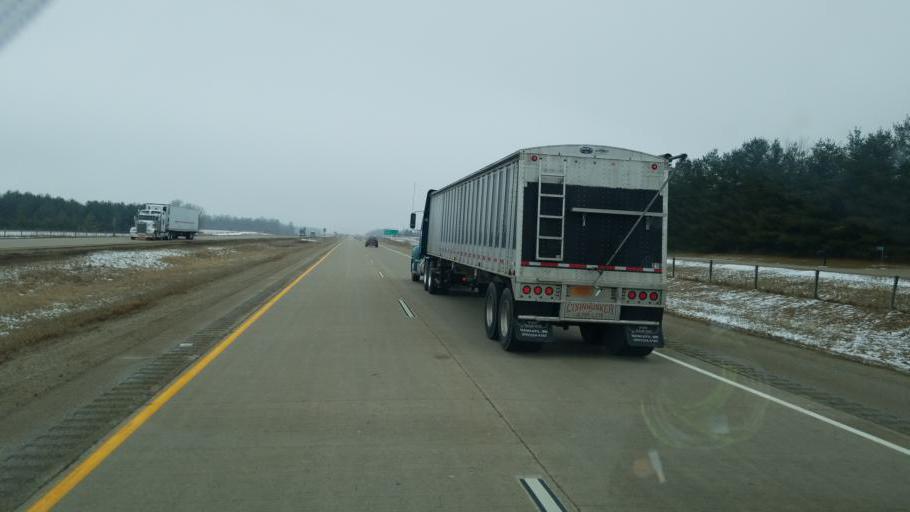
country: US
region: Wisconsin
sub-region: Winnebago County
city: Winneconne
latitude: 44.2343
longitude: -88.7506
